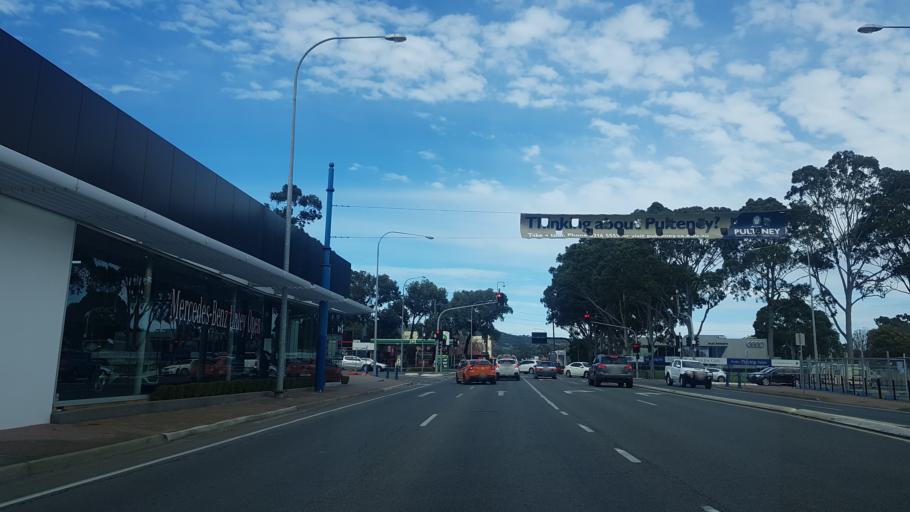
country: AU
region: South Australia
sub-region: Unley
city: Unley Park
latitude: -34.9647
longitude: 138.6086
